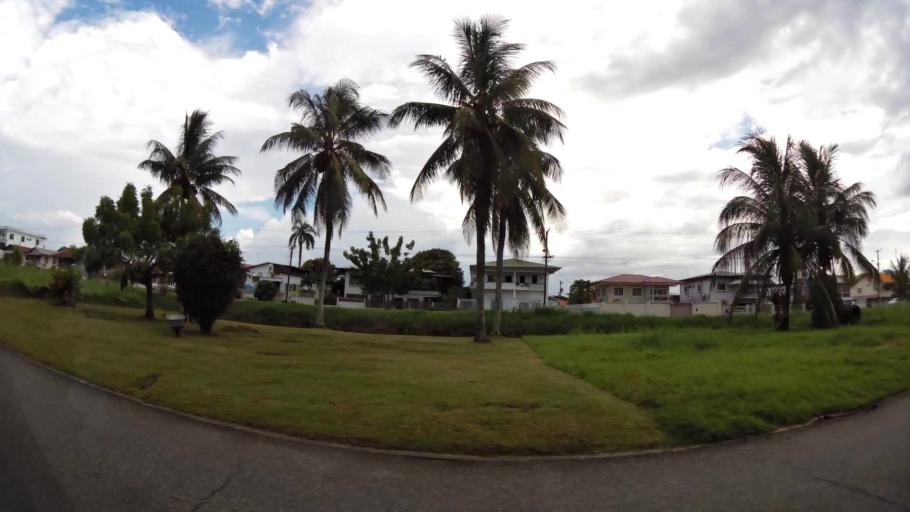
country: SR
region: Paramaribo
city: Paramaribo
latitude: 5.8400
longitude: -55.1383
